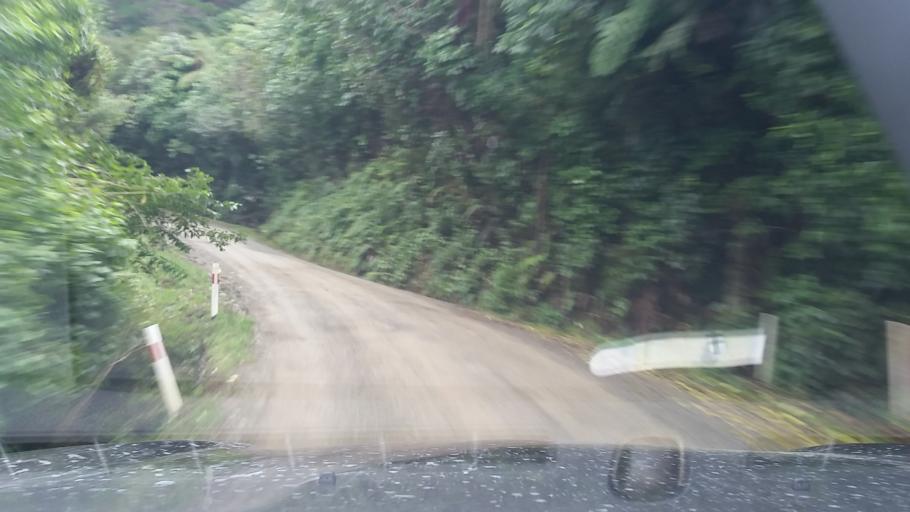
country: NZ
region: Marlborough
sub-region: Marlborough District
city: Picton
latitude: -41.1803
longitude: 174.0018
